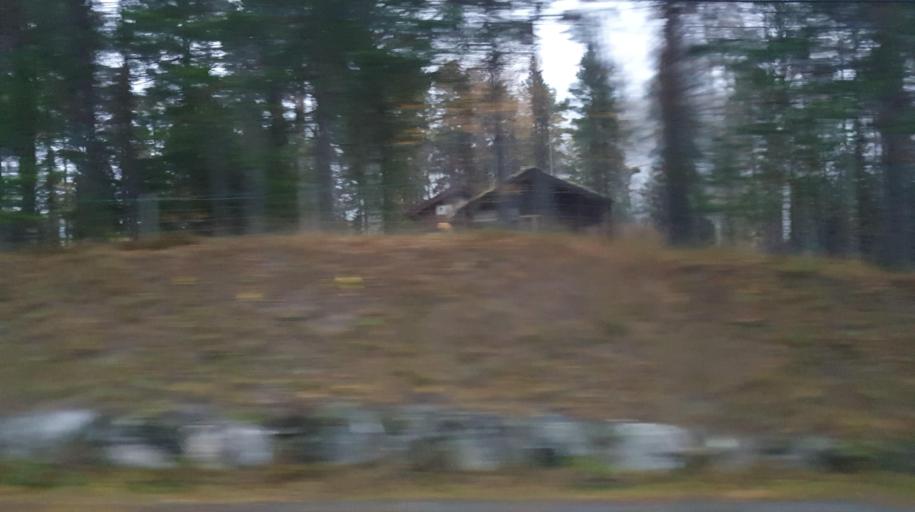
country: NO
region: Buskerud
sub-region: Krodsherad
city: Noresund
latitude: 60.1829
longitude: 9.6172
